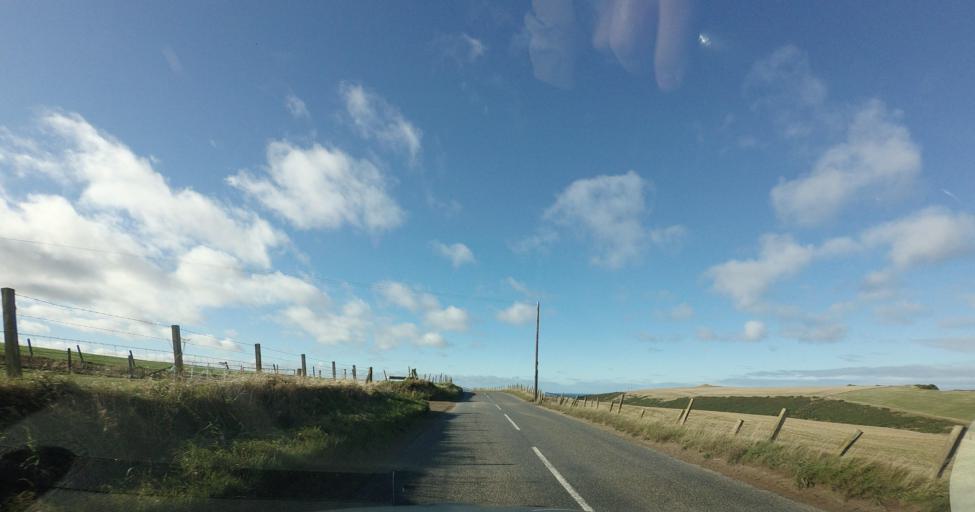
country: GB
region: Scotland
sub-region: Aberdeenshire
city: Macduff
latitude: 57.6644
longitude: -2.4001
